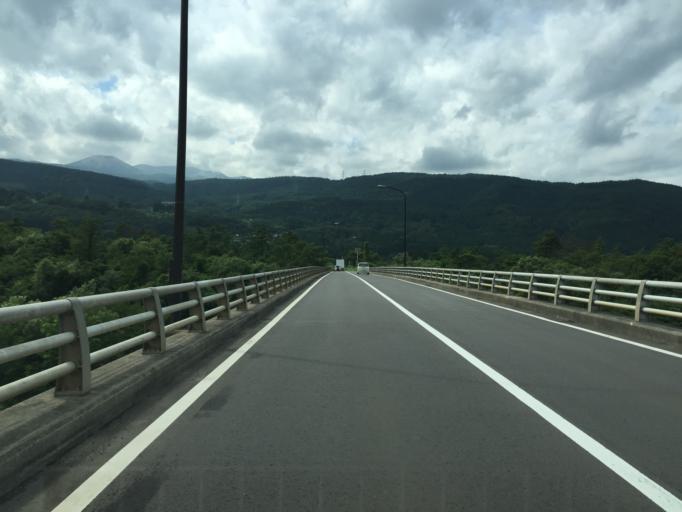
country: JP
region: Fukushima
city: Fukushima-shi
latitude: 37.7099
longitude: 140.3565
